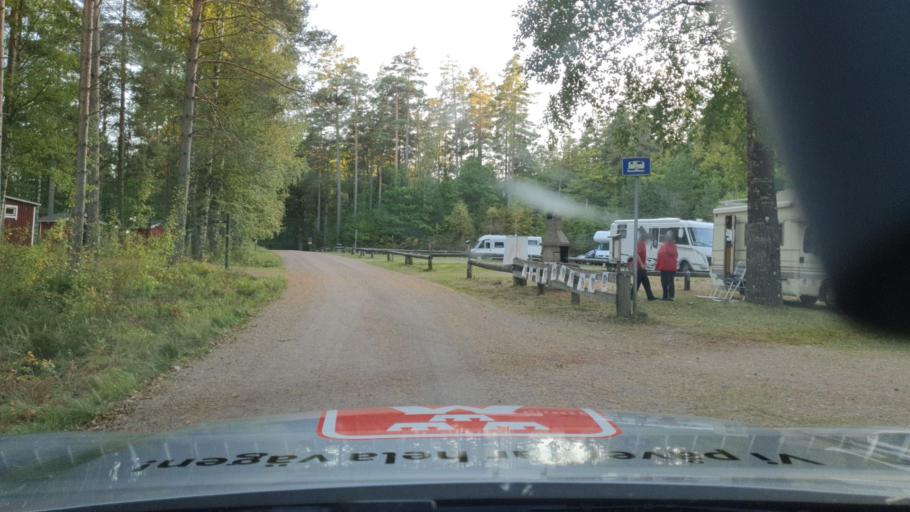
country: SE
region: Kalmar
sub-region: Hultsfreds Kommun
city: Malilla
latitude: 57.4559
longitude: 15.7252
